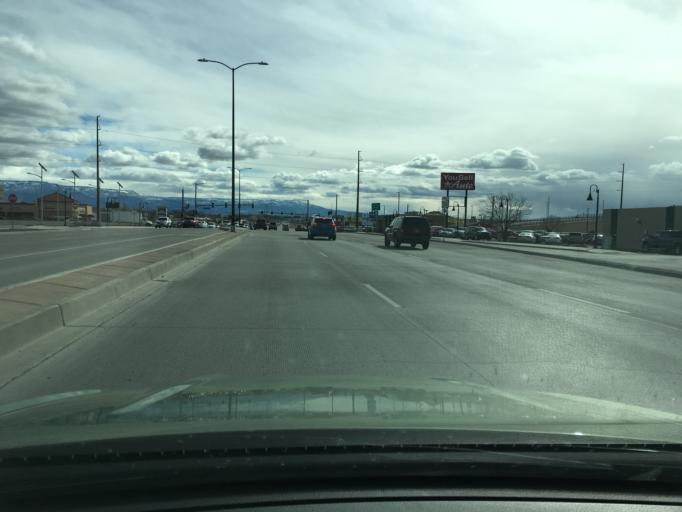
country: US
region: Colorado
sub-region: Mesa County
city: Redlands
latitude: 39.0838
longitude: -108.5914
